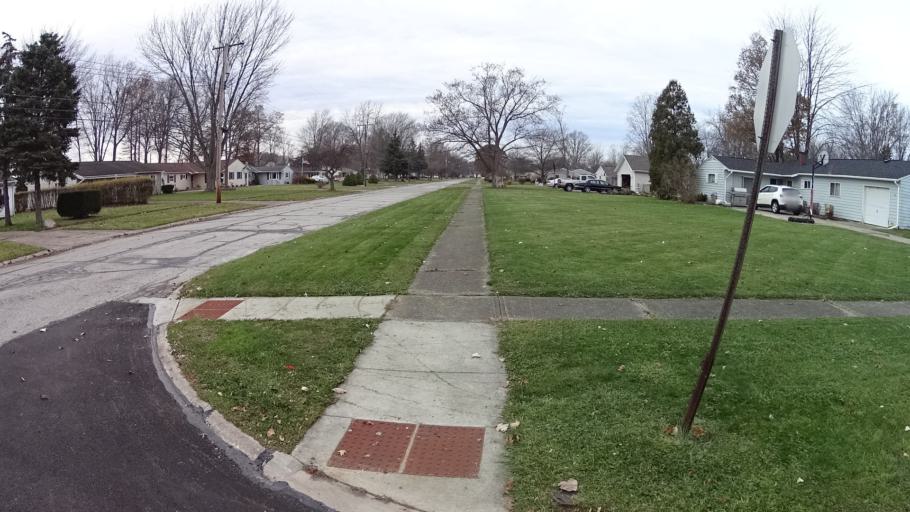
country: US
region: Ohio
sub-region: Lorain County
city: North Ridgeville
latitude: 41.3827
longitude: -81.9951
